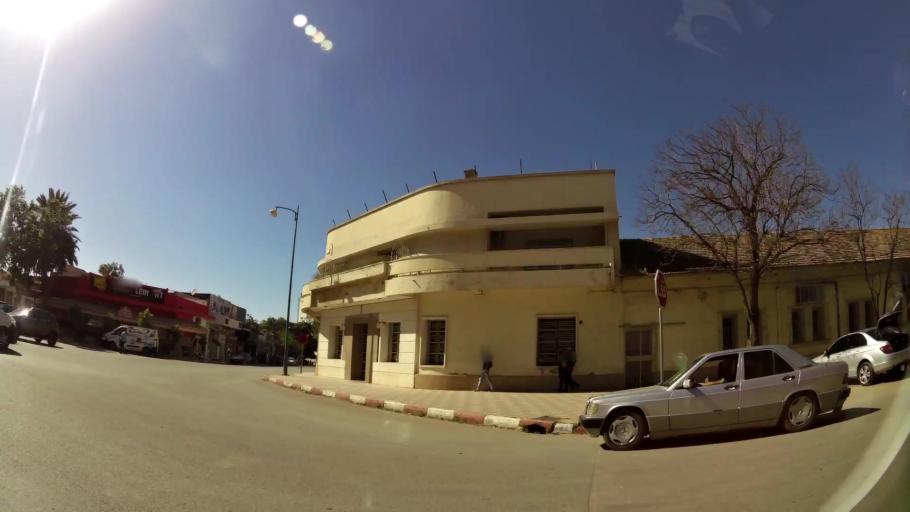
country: MA
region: Meknes-Tafilalet
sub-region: Meknes
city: Meknes
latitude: 33.8948
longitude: -5.5388
